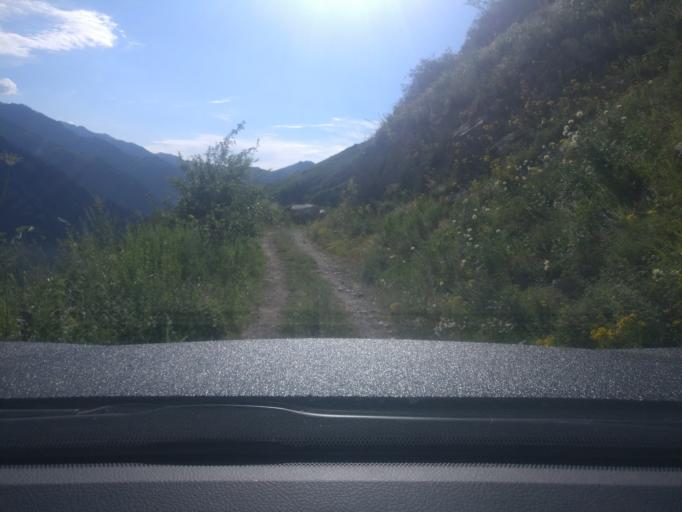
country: KZ
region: Almaty Qalasy
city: Almaty
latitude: 43.1072
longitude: 76.9415
